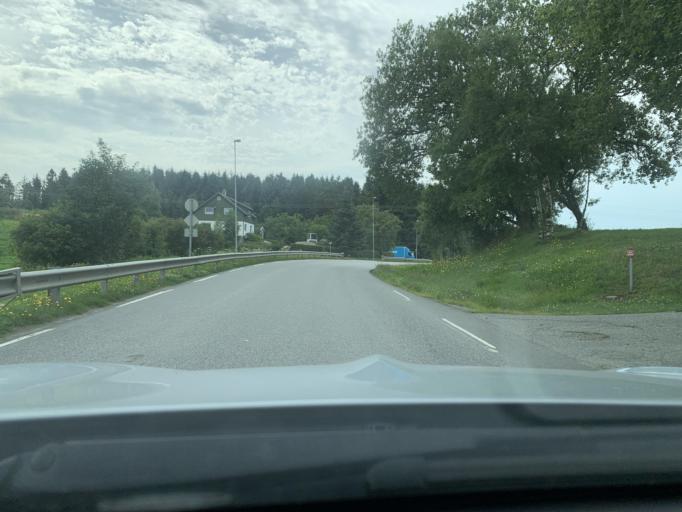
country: NO
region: Rogaland
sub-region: Time
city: Bryne
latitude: 58.7381
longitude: 5.6867
